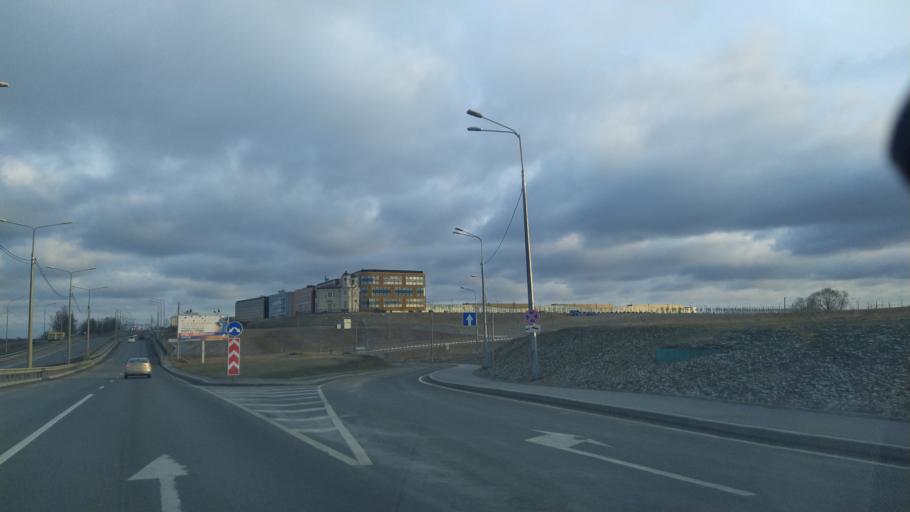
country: RU
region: St.-Petersburg
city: Aleksandrovskaya
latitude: 59.7679
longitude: 30.3482
